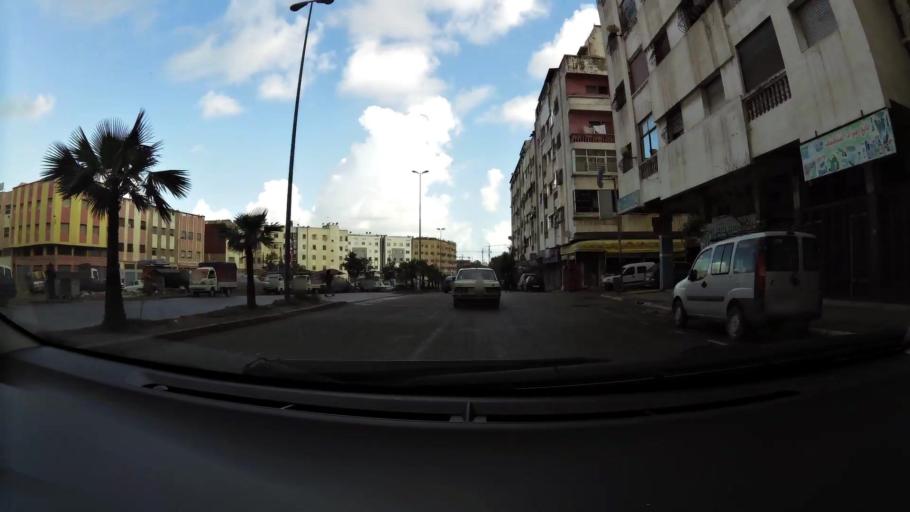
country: MA
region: Grand Casablanca
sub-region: Mediouna
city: Tit Mellil
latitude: 33.5853
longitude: -7.5253
